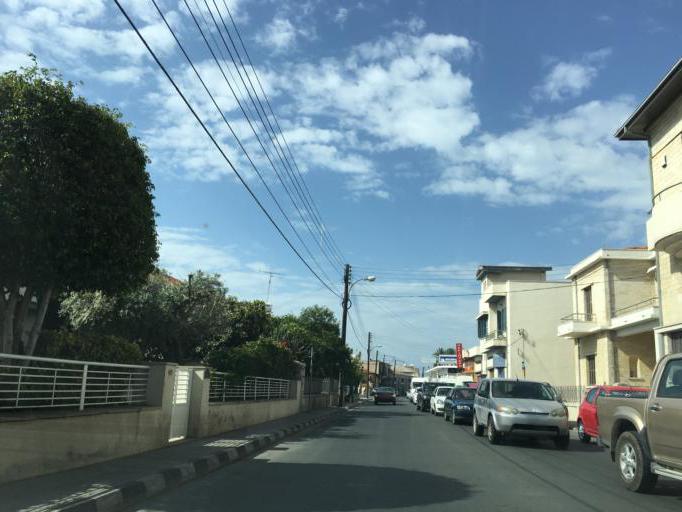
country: CY
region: Limassol
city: Limassol
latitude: 34.6765
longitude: 33.0388
